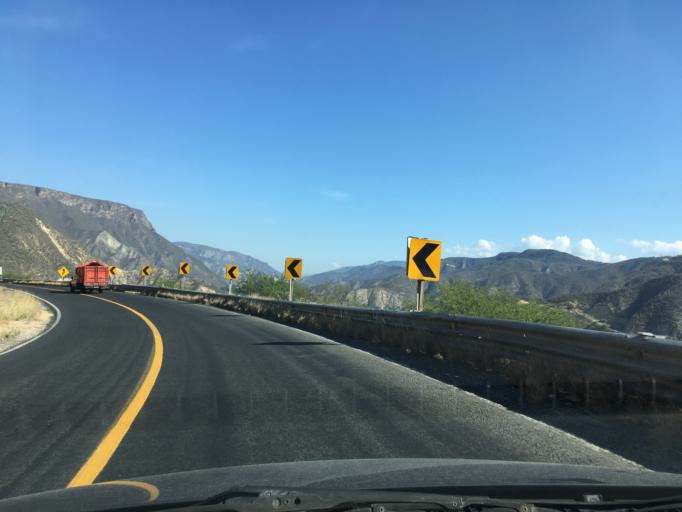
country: MX
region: Hidalgo
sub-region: San Agustin Metzquititlan
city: Mezquititlan
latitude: 20.4660
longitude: -98.6730
